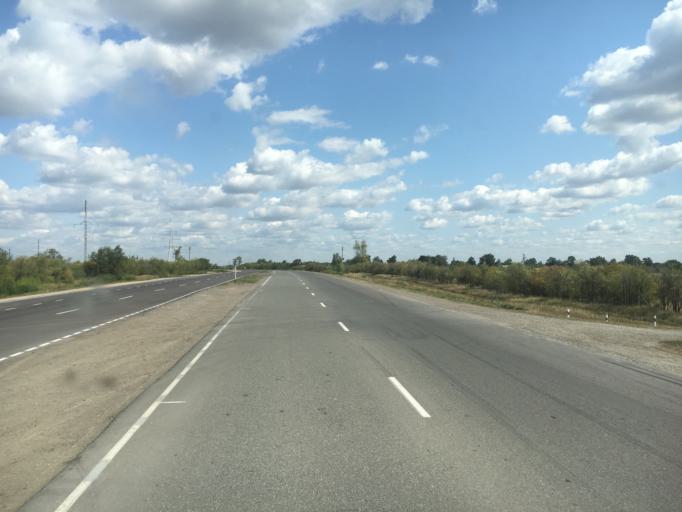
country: KZ
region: Qostanay
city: Kostanay
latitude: 53.1191
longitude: 63.5436
